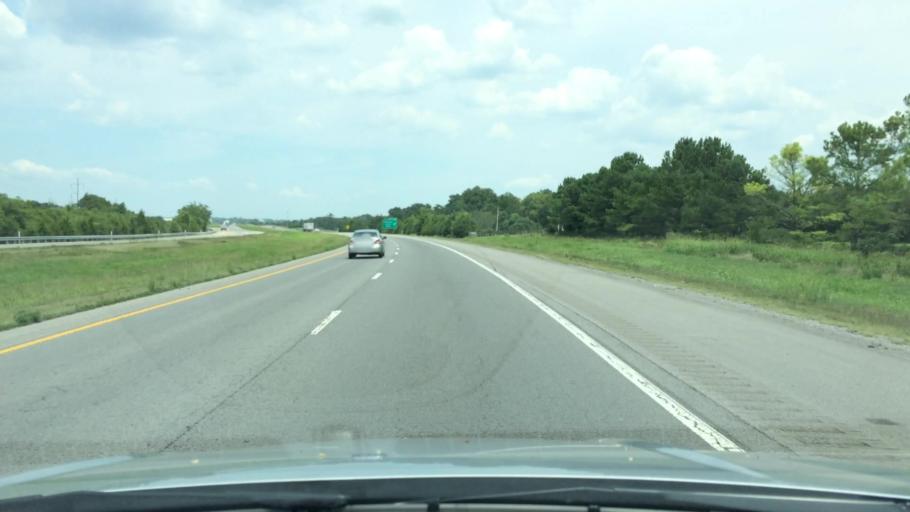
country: US
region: Tennessee
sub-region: Wilson County
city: Rural Hill
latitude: 36.1045
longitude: -86.4112
